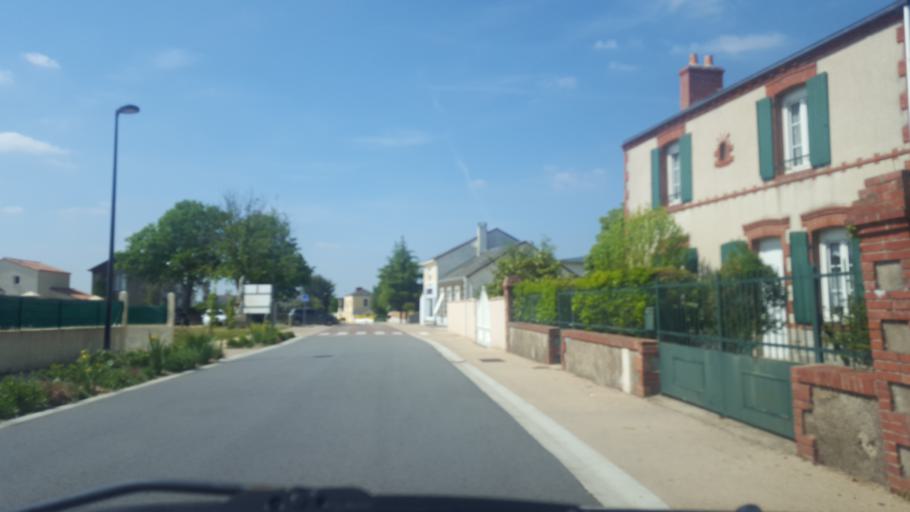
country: FR
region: Pays de la Loire
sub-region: Departement de la Loire-Atlantique
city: La Limouziniere
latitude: 46.9622
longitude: -1.5745
